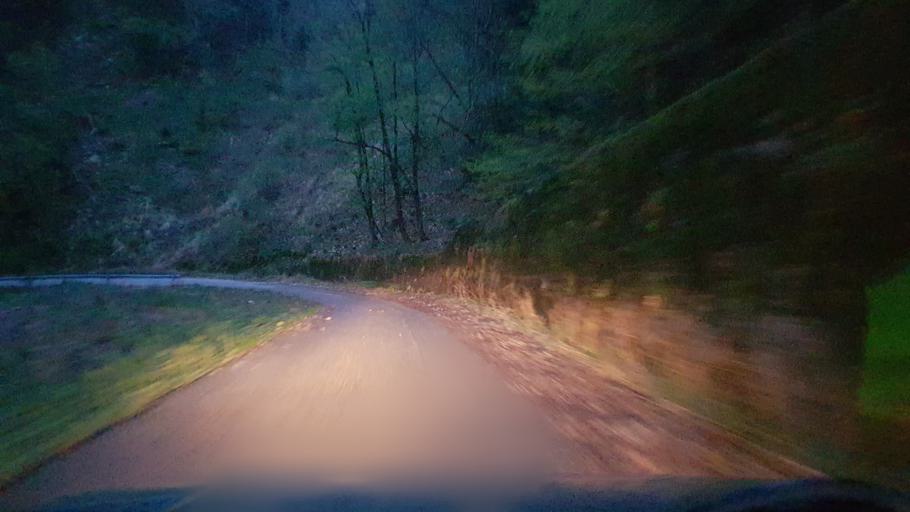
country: IT
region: Friuli Venezia Giulia
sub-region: Provincia di Udine
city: Taipana
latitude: 46.2425
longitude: 13.3556
